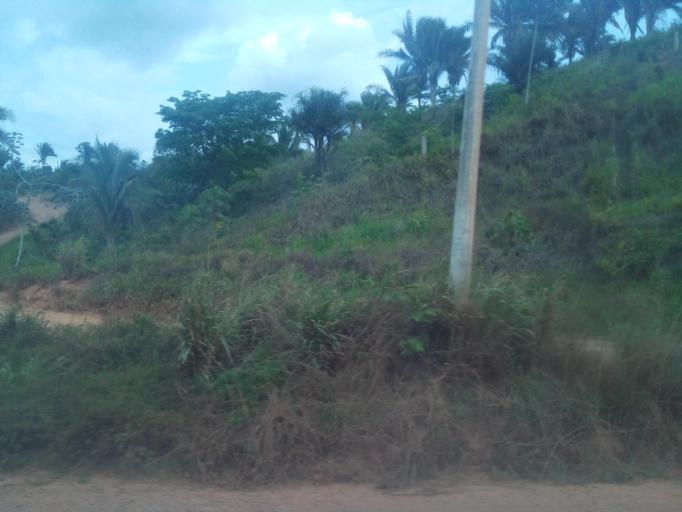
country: BR
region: Maranhao
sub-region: Santa Ines
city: Santa Ines
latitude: -3.7337
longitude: -46.1060
